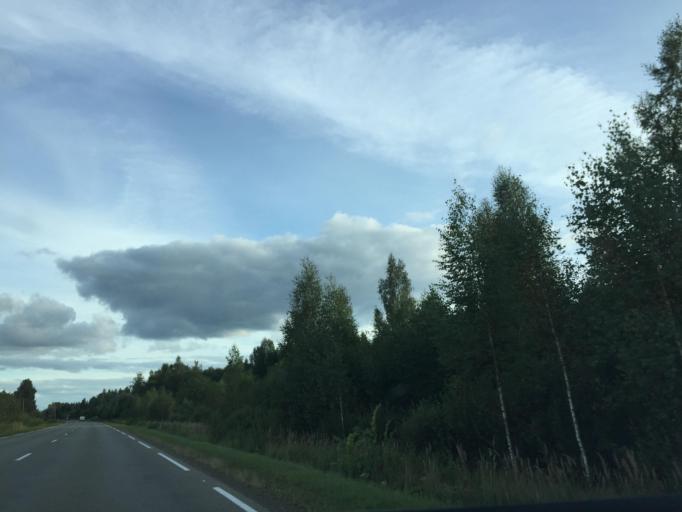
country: LV
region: Nereta
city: Nereta
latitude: 56.3126
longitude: 25.0970
